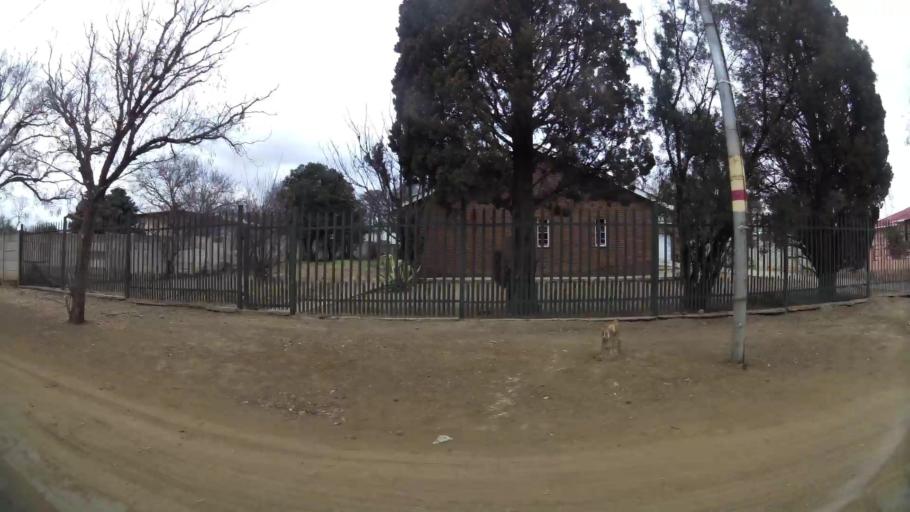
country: ZA
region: Orange Free State
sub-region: Fezile Dabi District Municipality
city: Kroonstad
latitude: -27.6832
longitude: 27.2291
